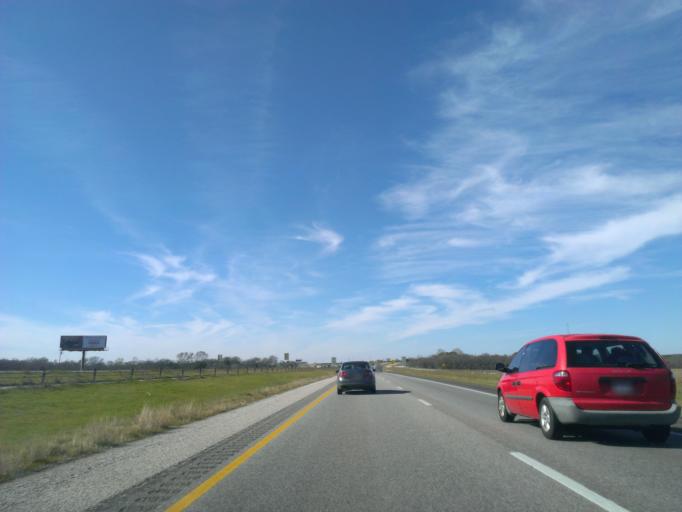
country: US
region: Texas
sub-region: Bell County
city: Nolanville
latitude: 31.0648
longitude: -97.5736
